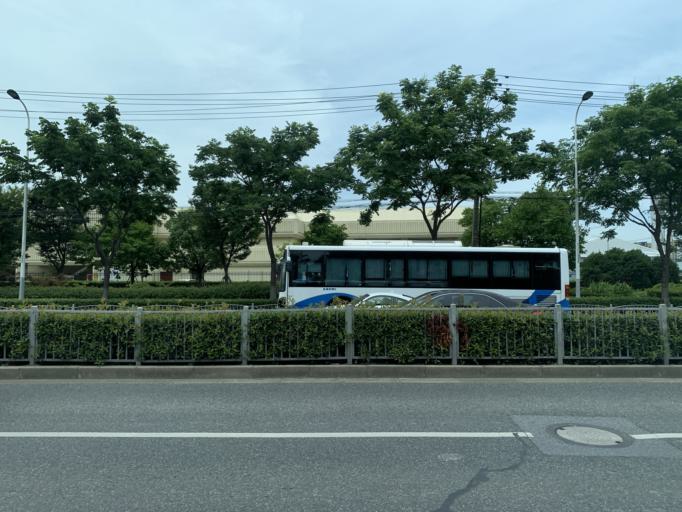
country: CN
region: Shanghai Shi
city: Kangqiao
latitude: 31.1583
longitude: 121.5601
